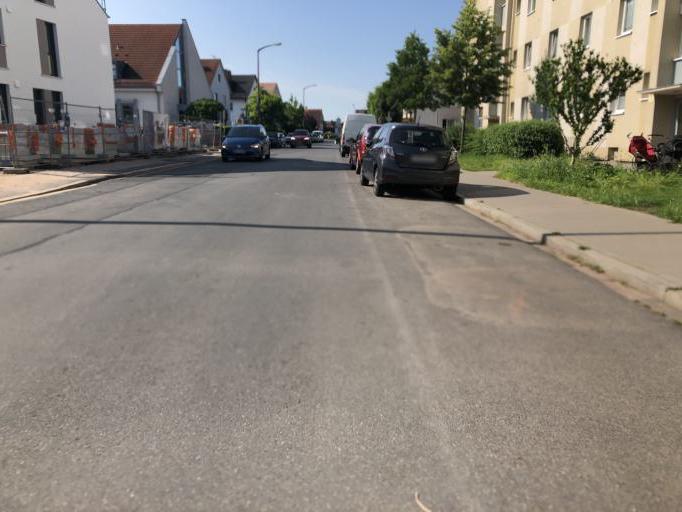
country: DE
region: Bavaria
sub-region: Regierungsbezirk Mittelfranken
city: Erlangen
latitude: 49.5676
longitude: 11.0008
